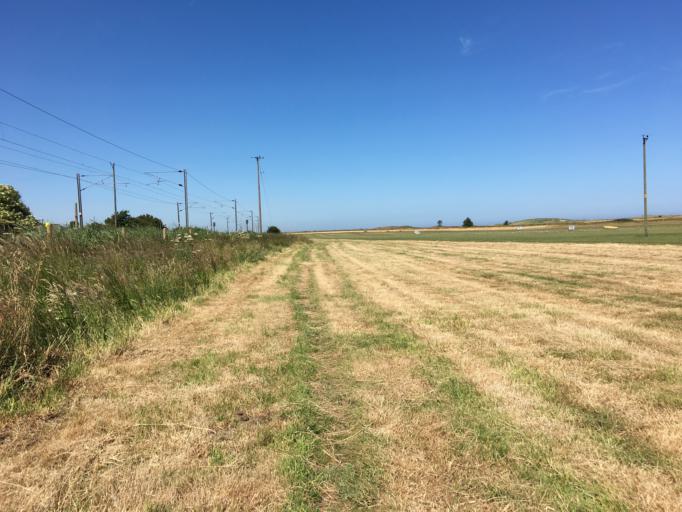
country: GB
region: England
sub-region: Northumberland
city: Ancroft
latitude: 55.7064
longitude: -1.9283
